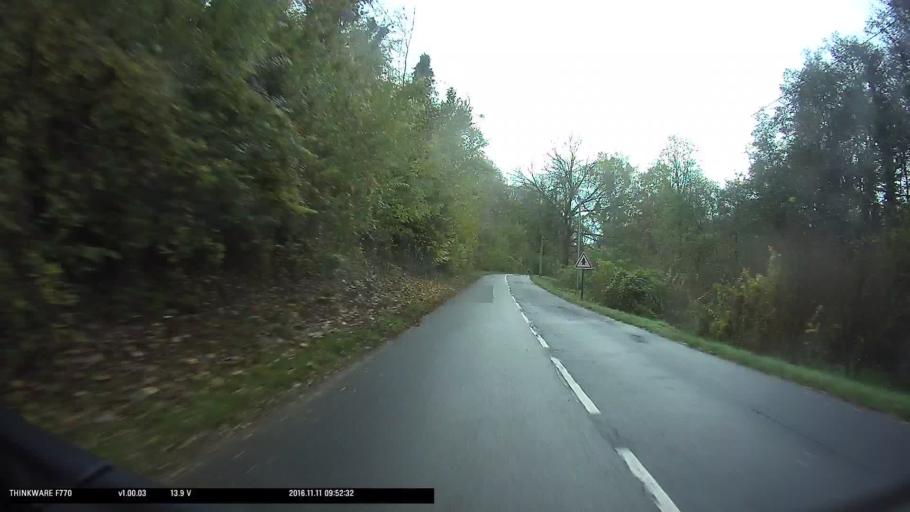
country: FR
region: Ile-de-France
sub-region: Departement du Val-d'Oise
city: Ableiges
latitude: 49.0851
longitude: 1.9981
